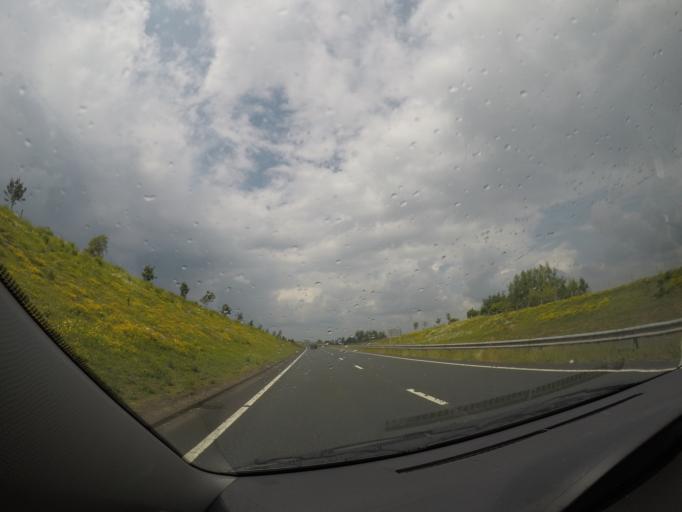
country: GB
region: England
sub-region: Cumbria
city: Appleby-in-Westmorland
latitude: 54.6419
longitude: -2.6166
